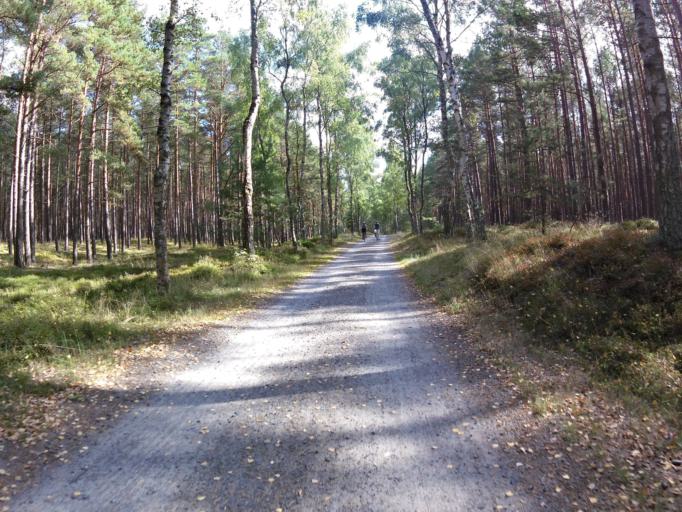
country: DE
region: Mecklenburg-Vorpommern
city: Karlshagen
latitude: 54.1003
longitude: 13.8605
